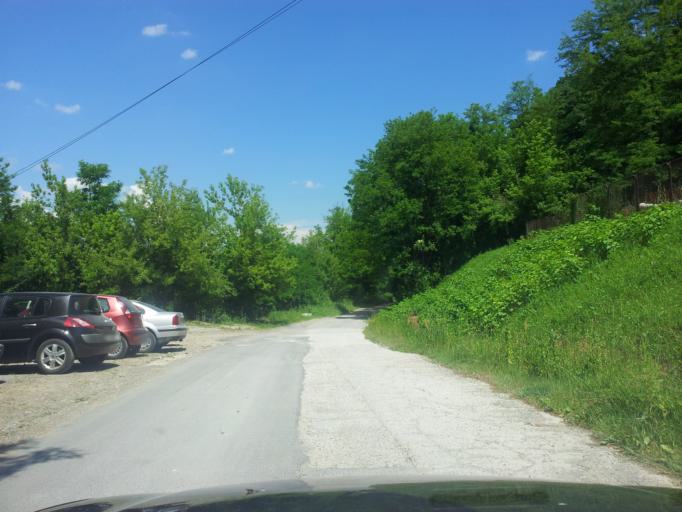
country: HR
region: Karlovacka
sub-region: Grad Karlovac
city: Karlovac
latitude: 45.4584
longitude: 15.5253
